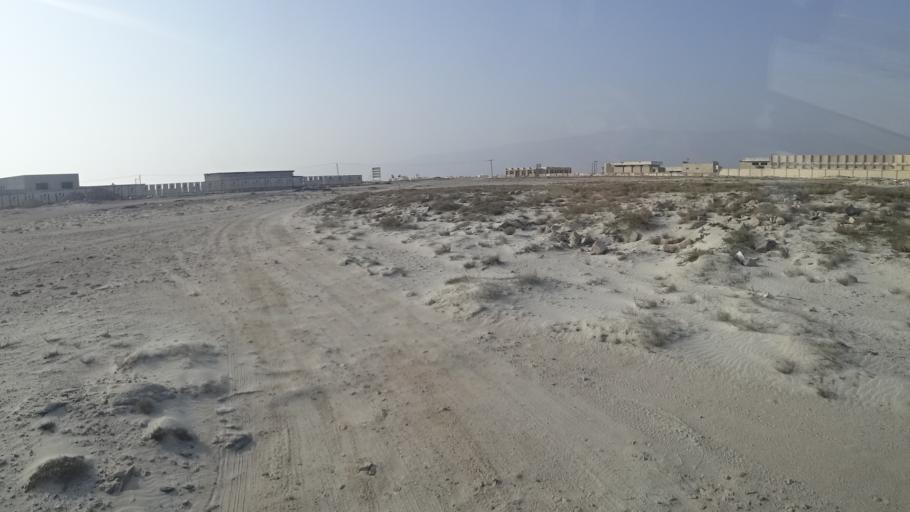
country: OM
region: Zufar
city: Salalah
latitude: 16.9703
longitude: 54.7030
